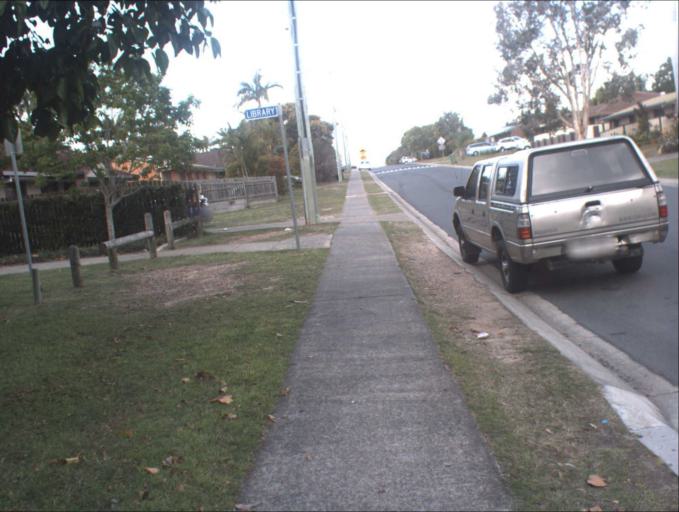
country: AU
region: Queensland
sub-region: Brisbane
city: Sunnybank Hills
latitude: -27.6659
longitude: 153.0426
